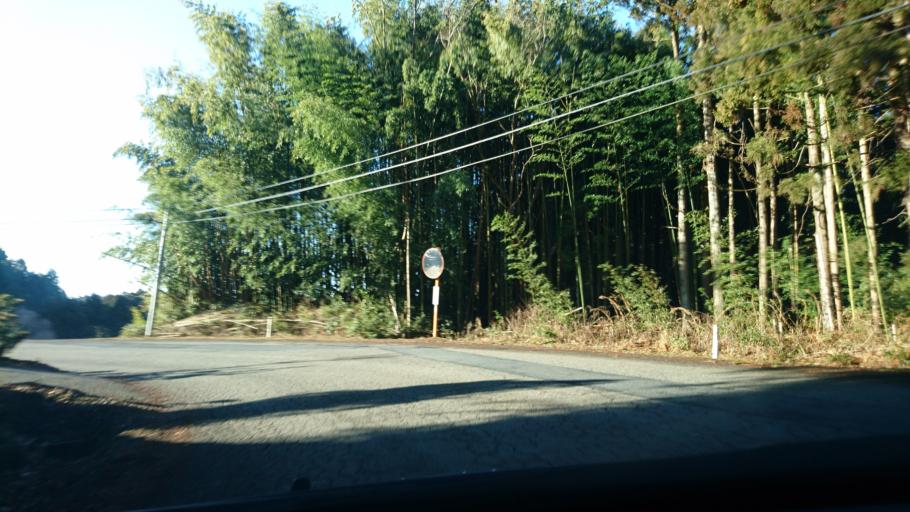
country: JP
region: Iwate
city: Ichinoseki
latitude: 38.8651
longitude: 141.2968
